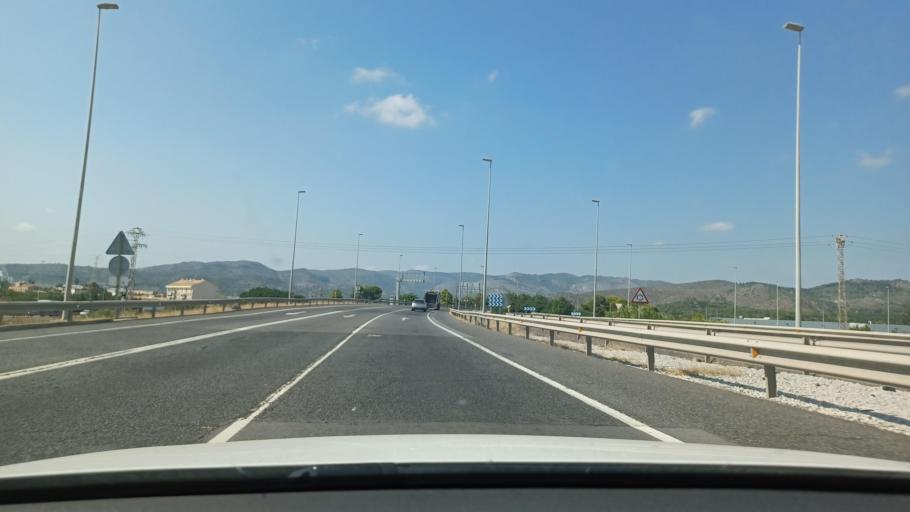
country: ES
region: Valencia
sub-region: Provincia de Castello
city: Borriol
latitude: 39.9917
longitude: -0.0896
